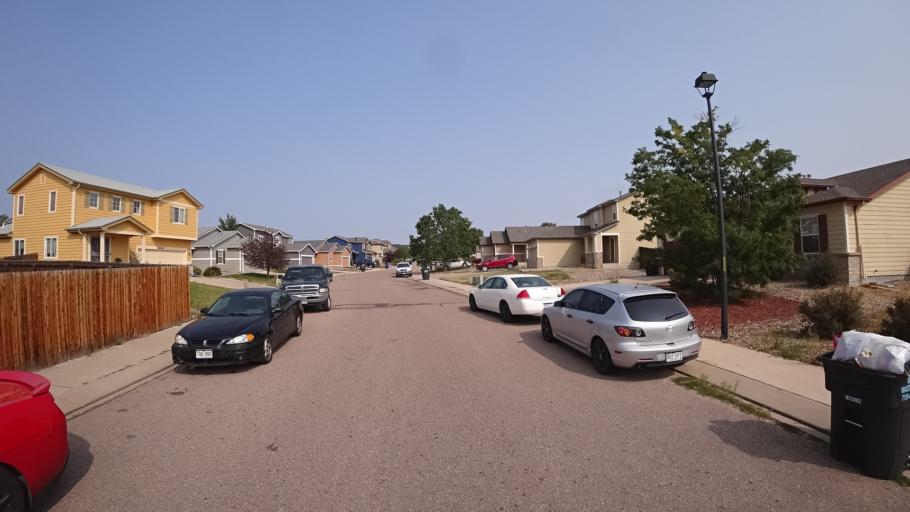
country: US
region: Colorado
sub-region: El Paso County
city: Stratmoor
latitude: 38.7968
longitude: -104.7621
